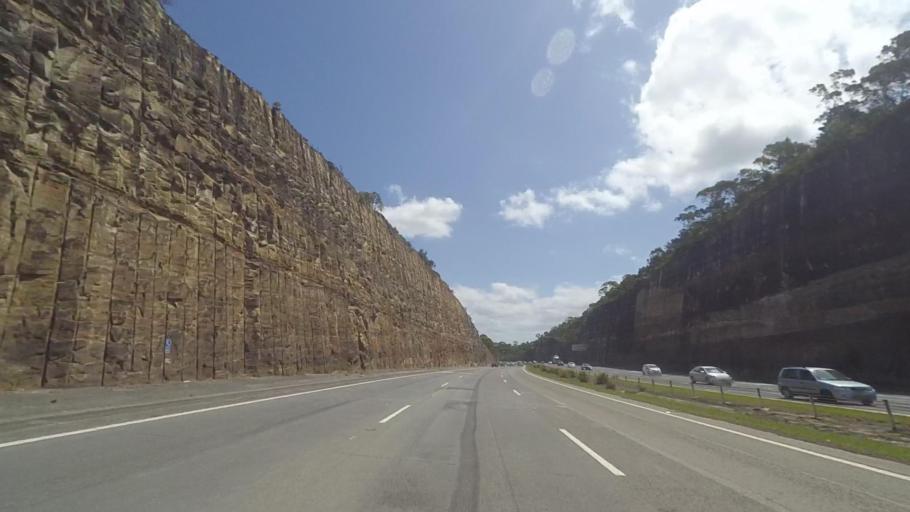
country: AU
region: New South Wales
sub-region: Hornsby Shire
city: Berowra
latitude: -33.6425
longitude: 151.1430
